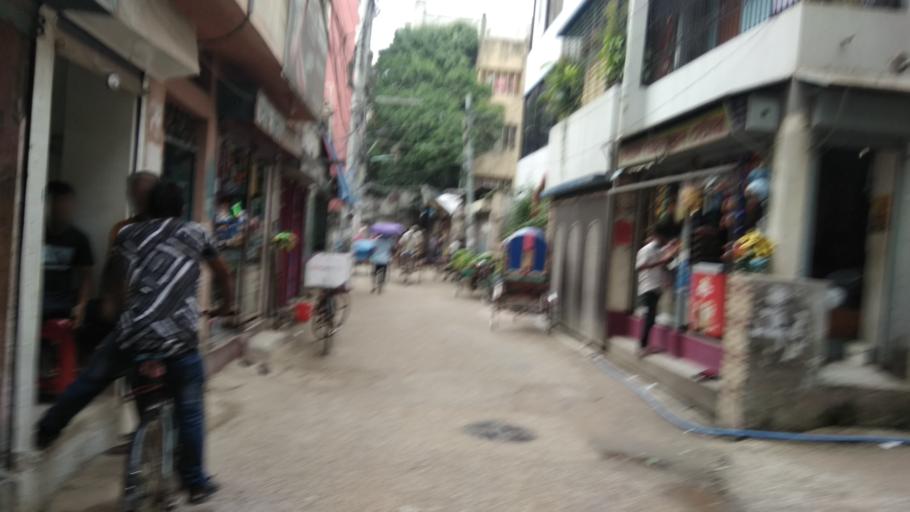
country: BD
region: Dhaka
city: Azimpur
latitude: 23.8010
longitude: 90.3731
